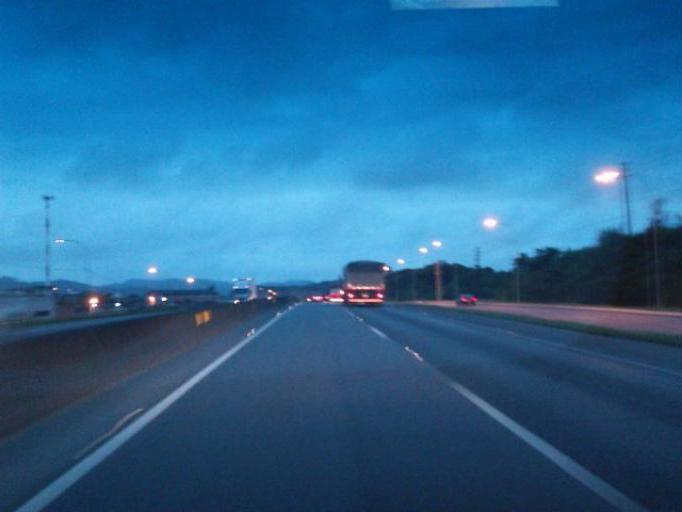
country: BR
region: Santa Catarina
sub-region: Penha
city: Penha
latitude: -26.7708
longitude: -48.6861
